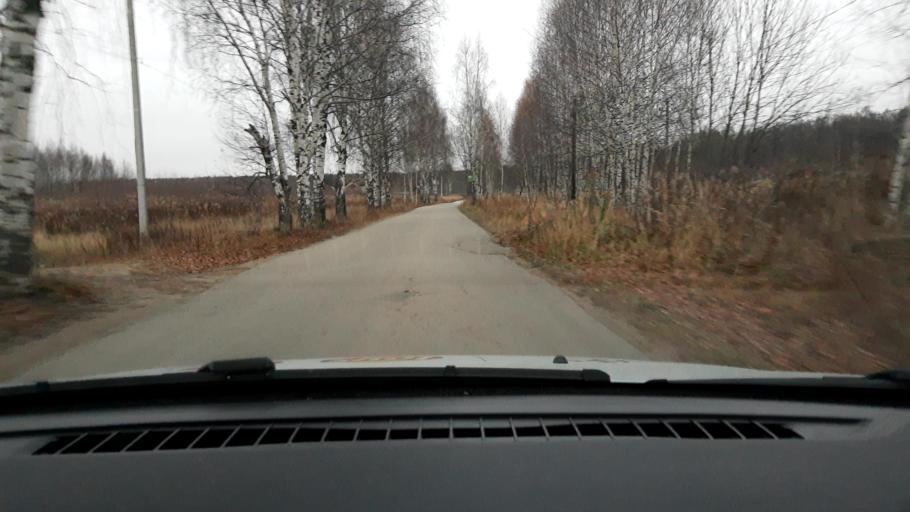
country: RU
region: Nizjnij Novgorod
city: Neklyudovo
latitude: 56.4148
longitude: 44.0147
